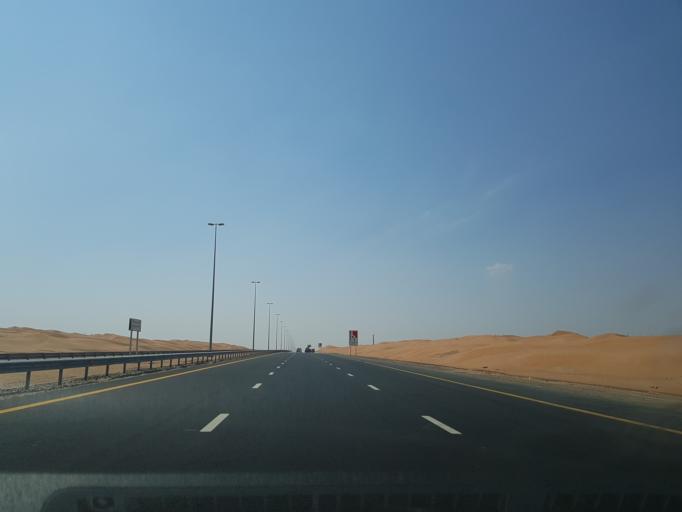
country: AE
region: Ash Shariqah
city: Adh Dhayd
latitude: 25.2493
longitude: 55.8112
